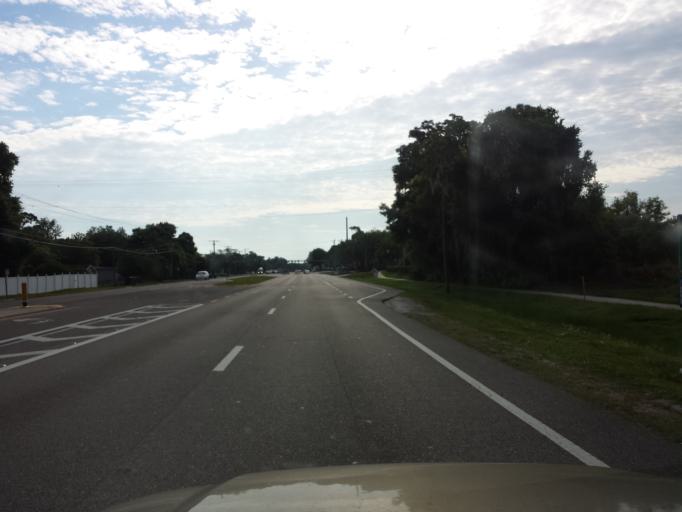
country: US
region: Florida
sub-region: Hillsborough County
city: Riverview
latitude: 27.8571
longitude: -82.3298
